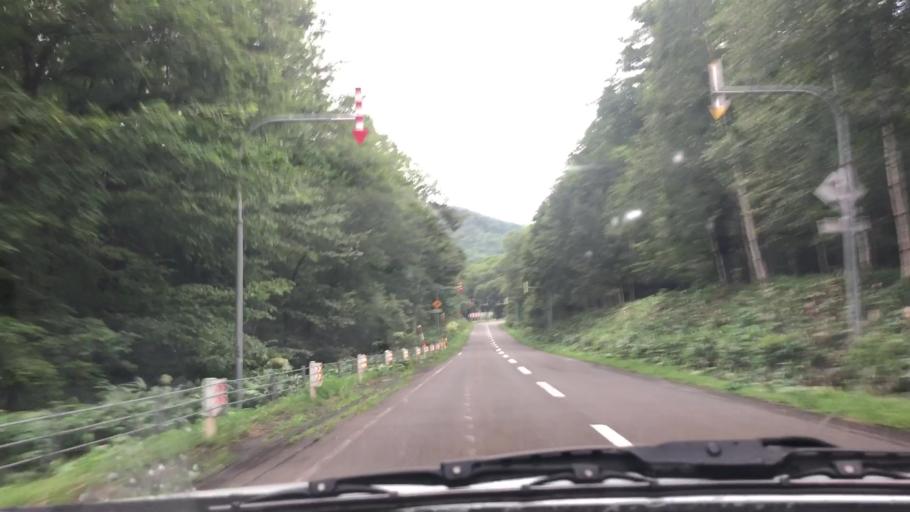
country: JP
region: Hokkaido
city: Shimo-furano
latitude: 42.9228
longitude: 142.3747
